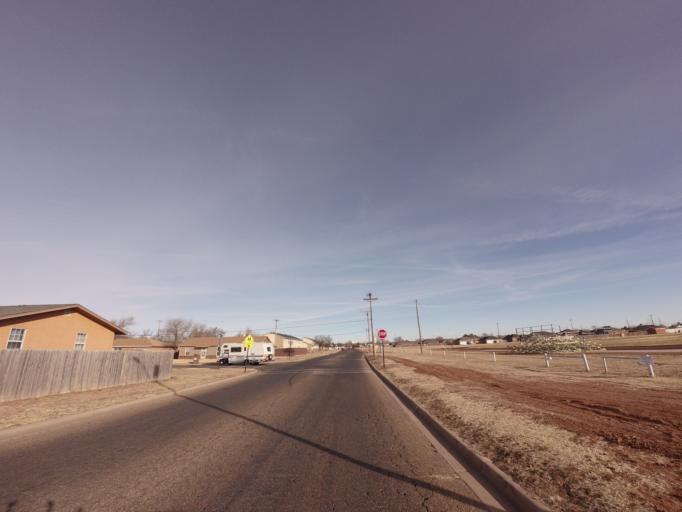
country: US
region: New Mexico
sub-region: Curry County
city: Clovis
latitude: 34.4115
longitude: -103.2272
